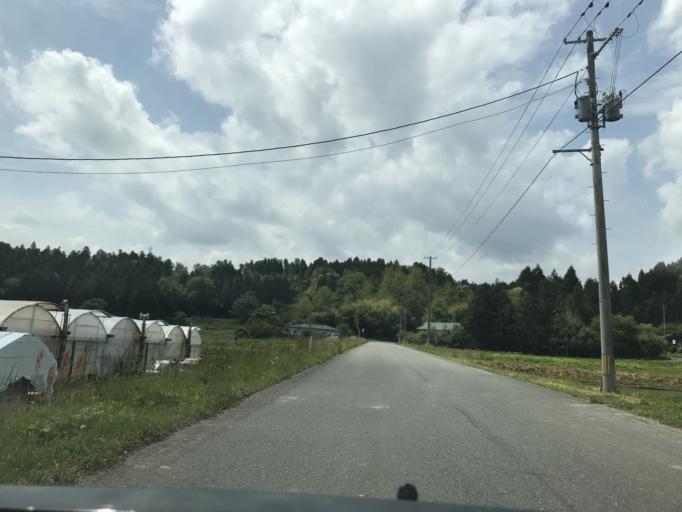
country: JP
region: Miyagi
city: Furukawa
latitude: 38.7396
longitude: 140.9306
